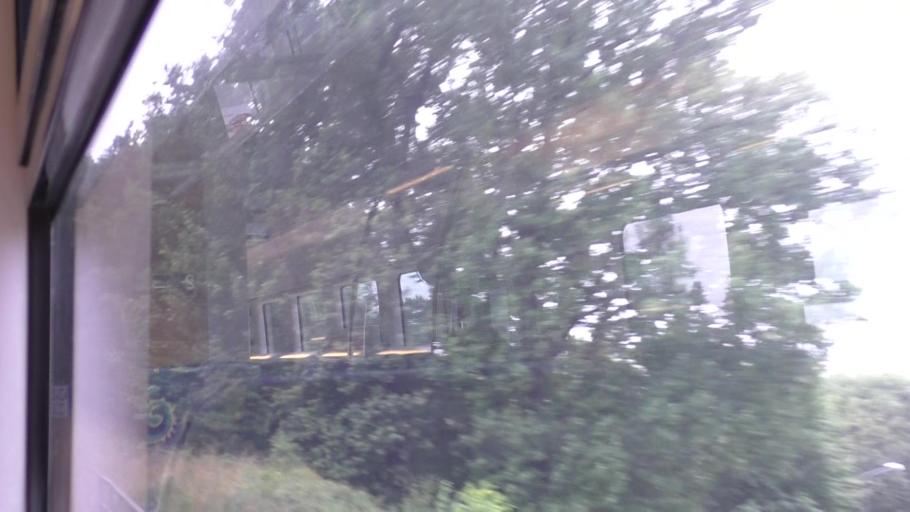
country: DE
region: Saxony
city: Goerlitz
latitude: 51.1743
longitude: 14.9662
